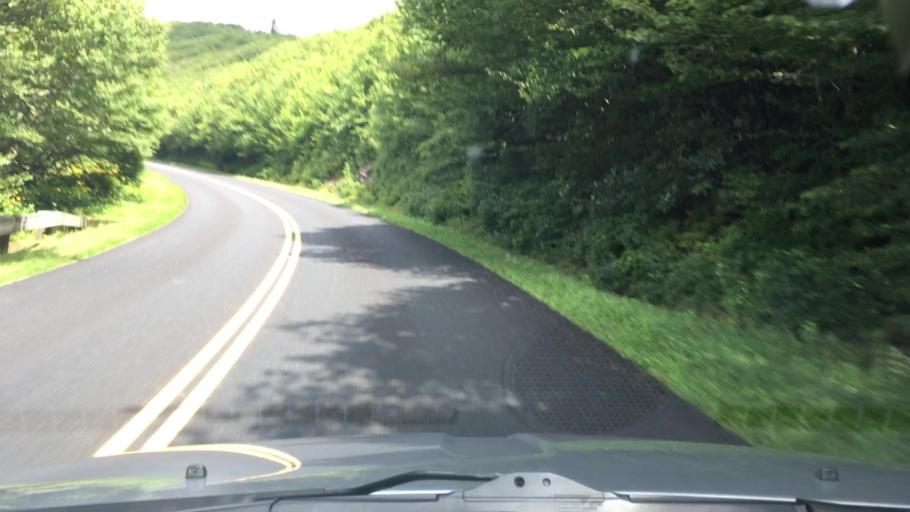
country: US
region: North Carolina
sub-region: Buncombe County
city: Black Mountain
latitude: 35.7183
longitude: -82.3581
